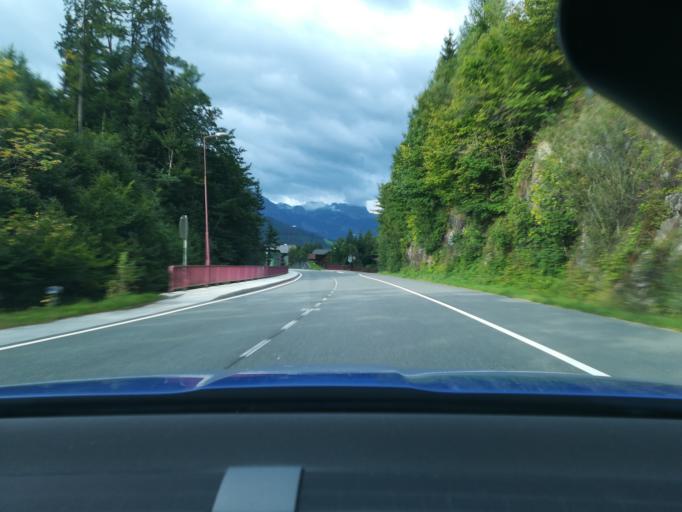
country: AT
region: Salzburg
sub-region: Politischer Bezirk Hallein
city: Abtenau
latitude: 47.5892
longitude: 13.4607
